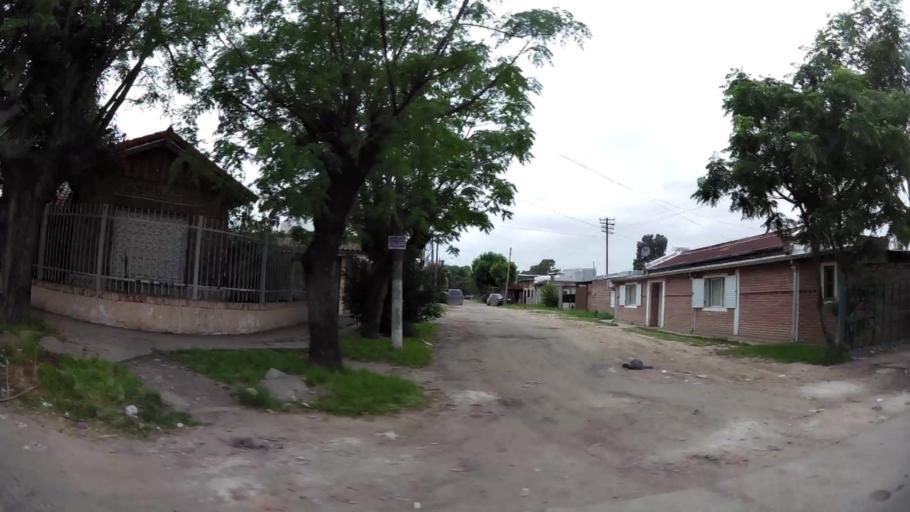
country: AR
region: Buenos Aires F.D.
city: Villa Lugano
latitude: -34.7111
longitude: -58.5166
